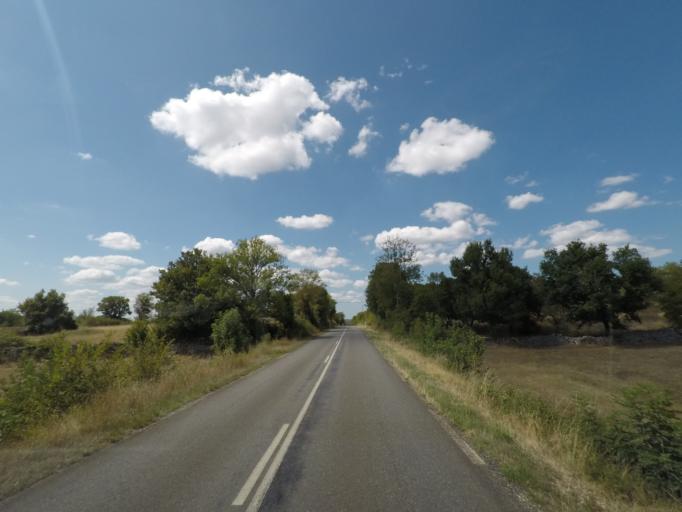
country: FR
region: Midi-Pyrenees
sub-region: Departement du Lot
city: Lacapelle-Marival
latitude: 44.6254
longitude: 1.8502
